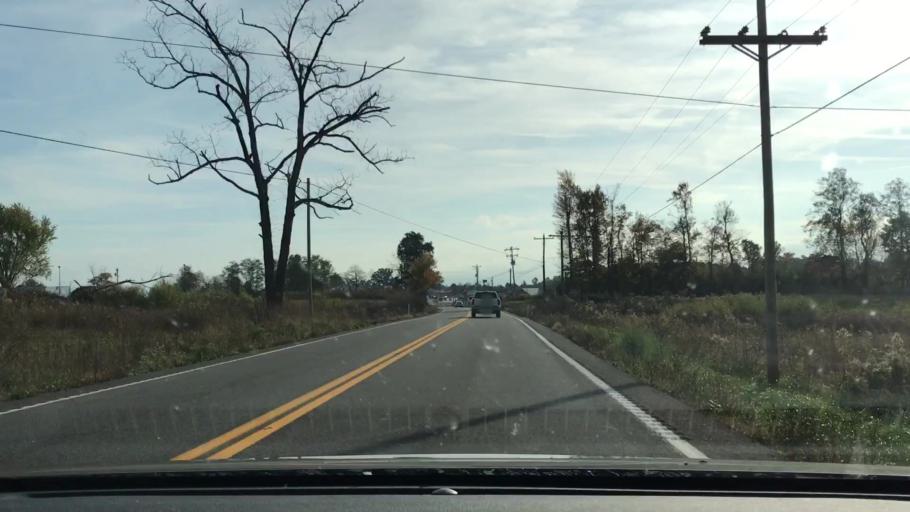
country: US
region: Tennessee
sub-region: Fentress County
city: Grimsley
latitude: 36.1855
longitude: -85.0243
